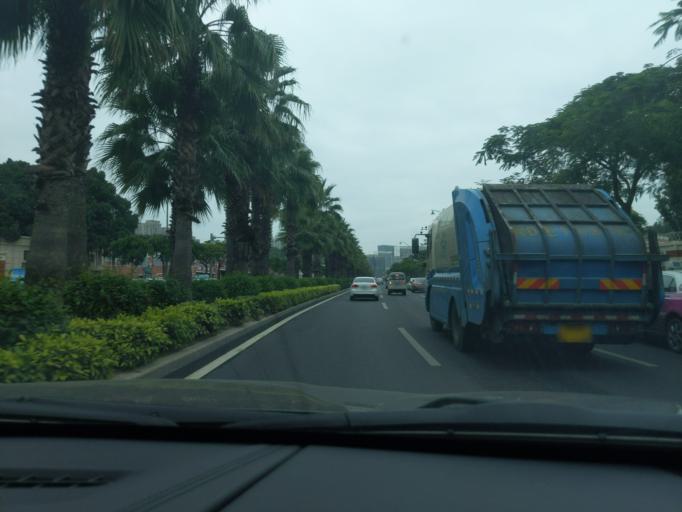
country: CN
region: Fujian
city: Liuwudian
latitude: 24.4965
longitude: 118.1703
